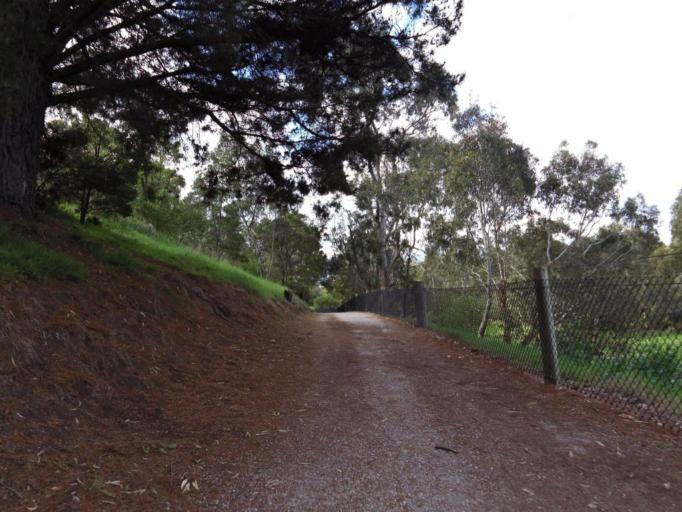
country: AU
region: Victoria
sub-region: Banyule
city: Viewbank
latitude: -37.7497
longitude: 145.0834
